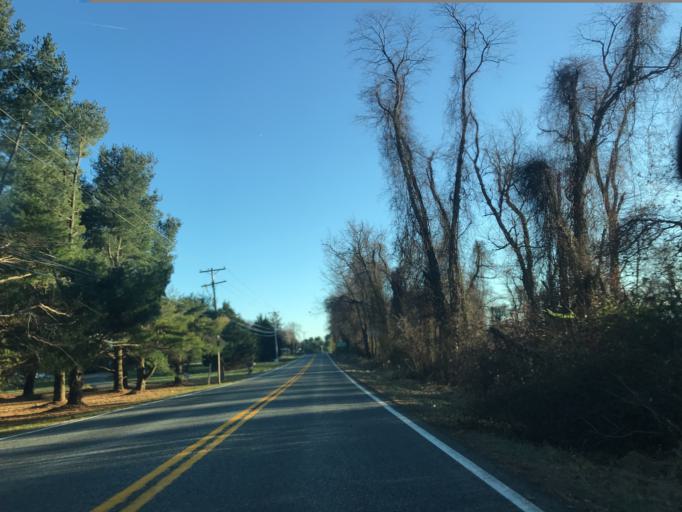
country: US
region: Maryland
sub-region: Harford County
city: Jarrettsville
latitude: 39.5793
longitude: -76.5008
